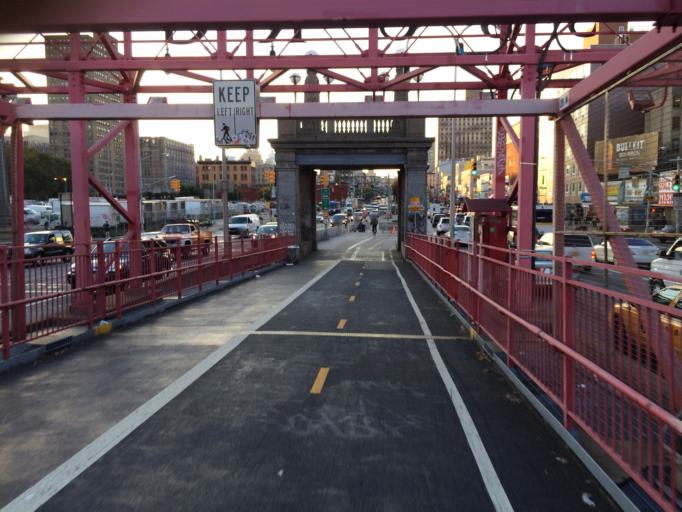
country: US
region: New York
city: New York City
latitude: 40.7175
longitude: -73.9852
